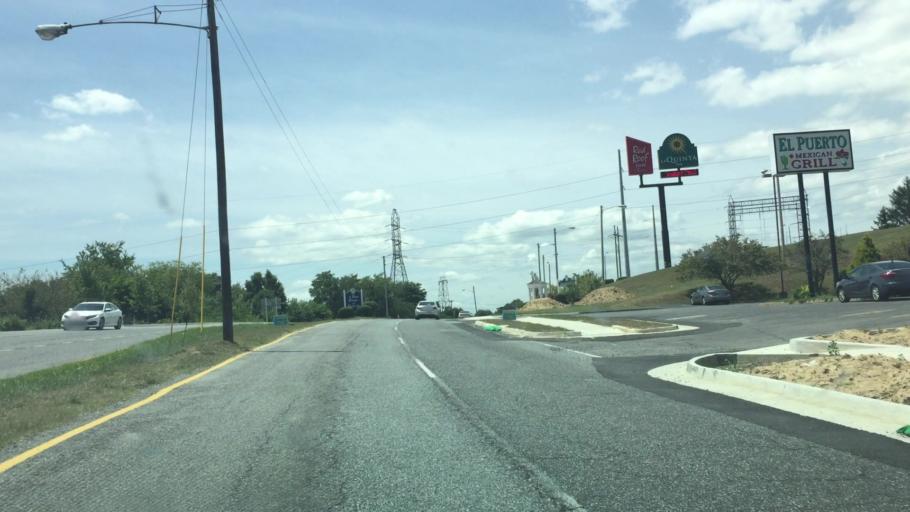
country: US
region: Virginia
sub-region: Wythe County
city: Wytheville
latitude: 36.9479
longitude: -81.0578
